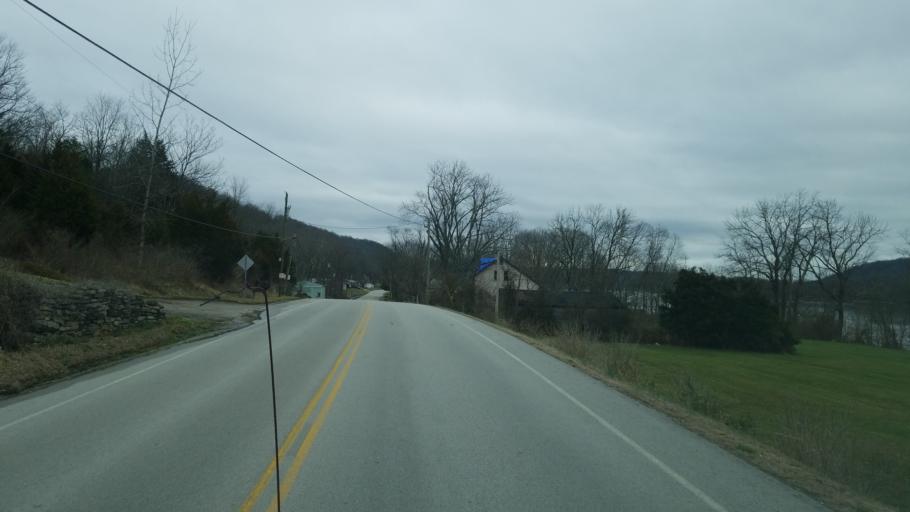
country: US
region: Ohio
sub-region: Brown County
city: Ripley
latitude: 38.7659
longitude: -83.8817
